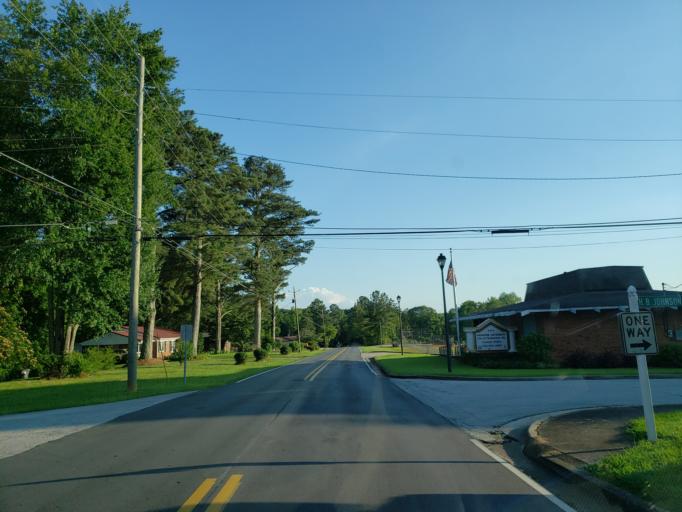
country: US
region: Georgia
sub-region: Haralson County
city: Tallapoosa
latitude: 33.7509
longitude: -85.2968
